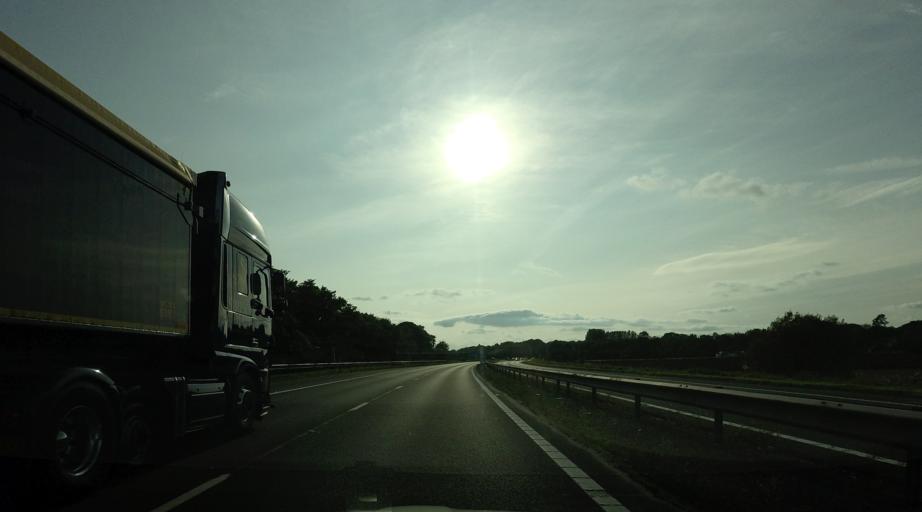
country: GB
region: Scotland
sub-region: Perth and Kinross
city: Milnathort
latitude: 56.2347
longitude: -3.3998
